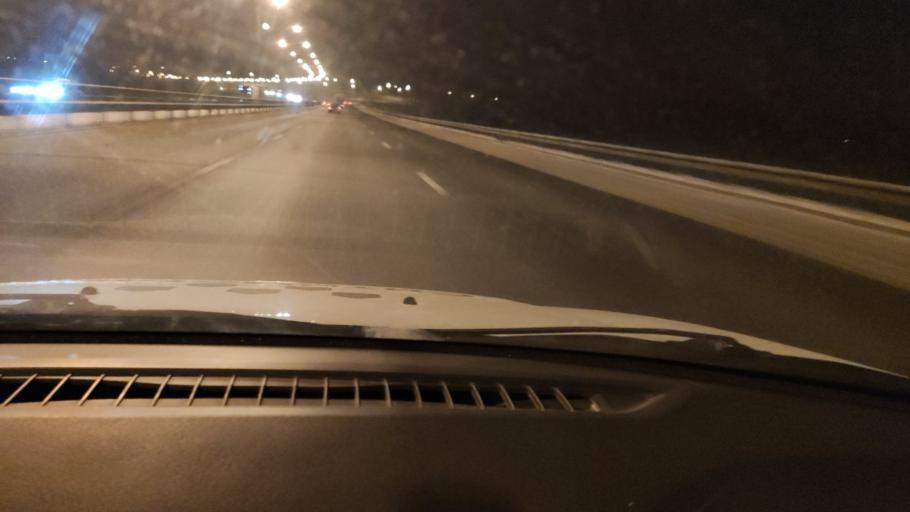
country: RU
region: Perm
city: Zvezdnyy
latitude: 57.7746
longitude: 56.3391
